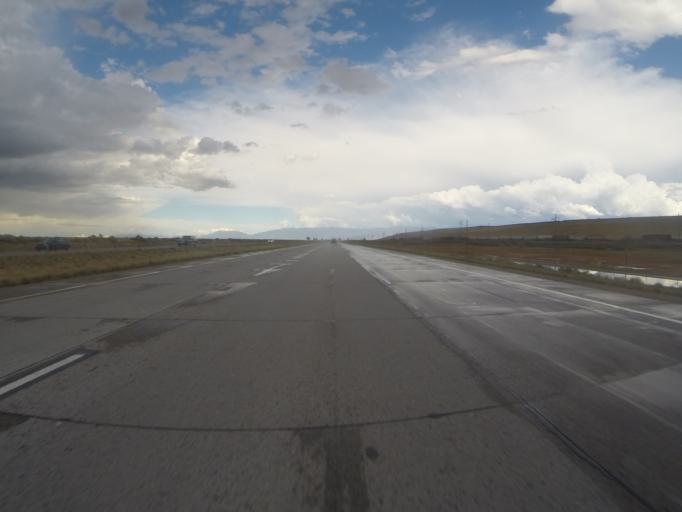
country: US
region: Utah
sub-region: Salt Lake County
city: Magna
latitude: 40.7513
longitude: -112.1755
